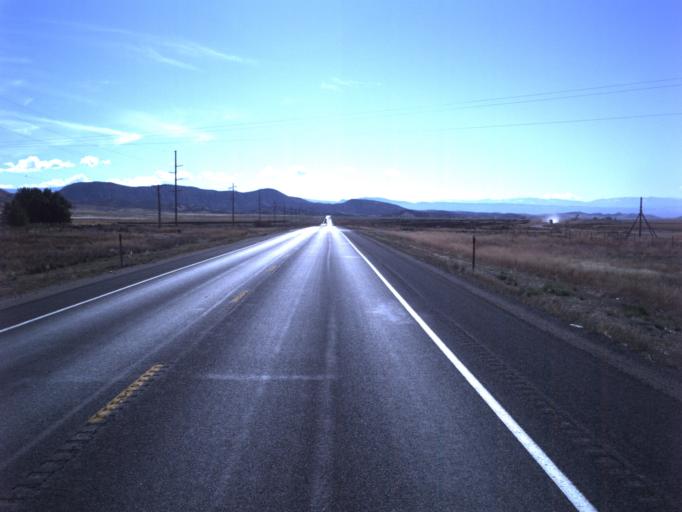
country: US
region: Utah
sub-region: Sanpete County
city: Gunnison
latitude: 39.2628
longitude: -111.8666
